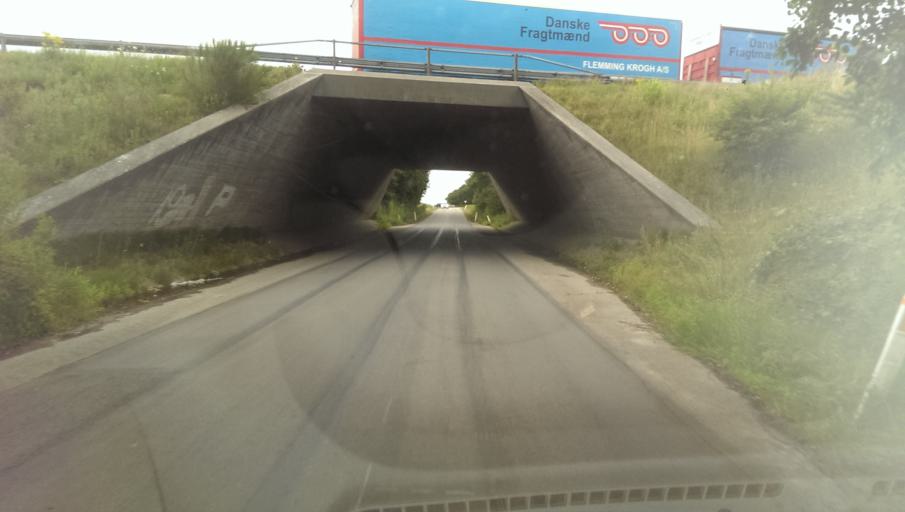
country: DK
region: South Denmark
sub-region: Esbjerg Kommune
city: Tjaereborg
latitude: 55.5173
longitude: 8.5258
